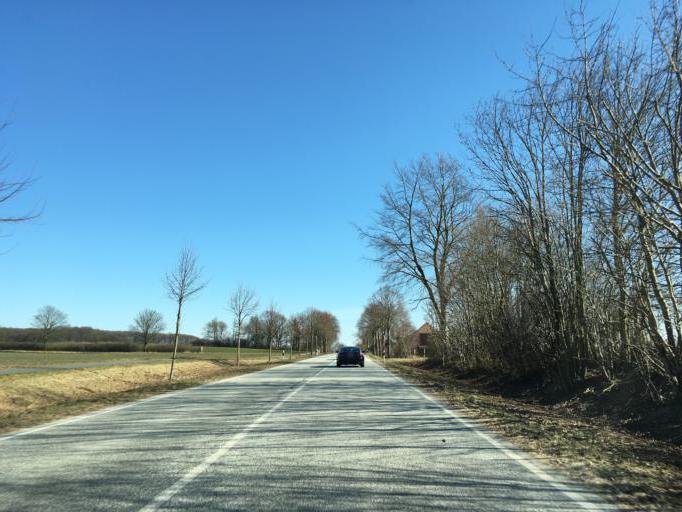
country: DE
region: Schleswig-Holstein
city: Kulpin
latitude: 53.7151
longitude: 10.6909
